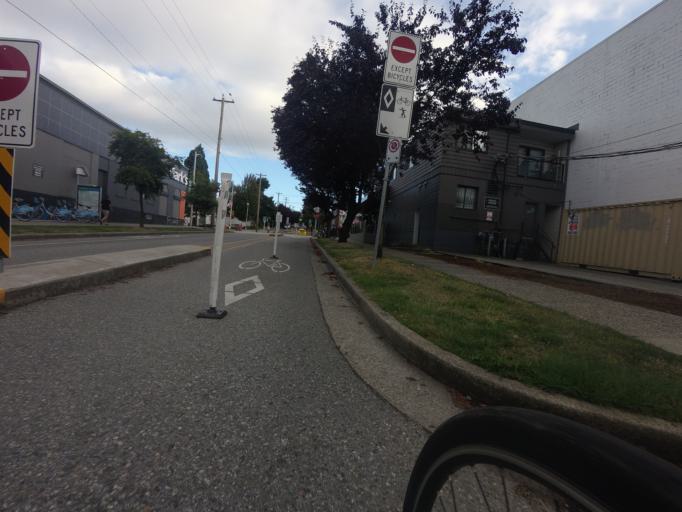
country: CA
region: British Columbia
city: West End
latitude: 49.2685
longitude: -123.1480
